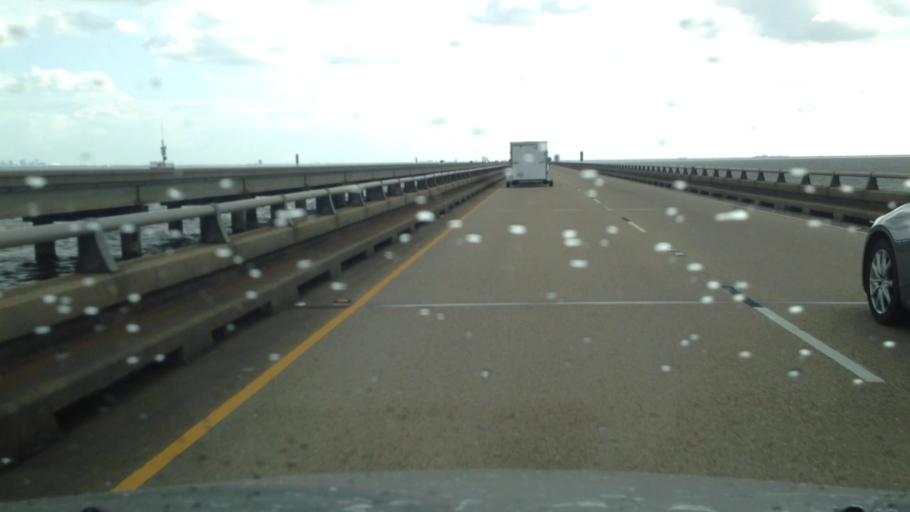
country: US
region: Louisiana
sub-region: Jefferson Parish
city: Metairie
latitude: 30.1063
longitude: -90.1393
